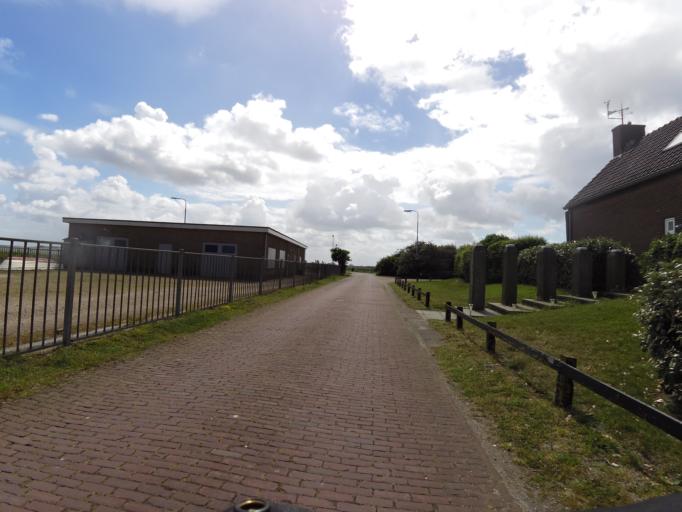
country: NL
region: Zeeland
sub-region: Schouwen-Duiveland
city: Bruinisse
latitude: 51.6510
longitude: 4.0980
